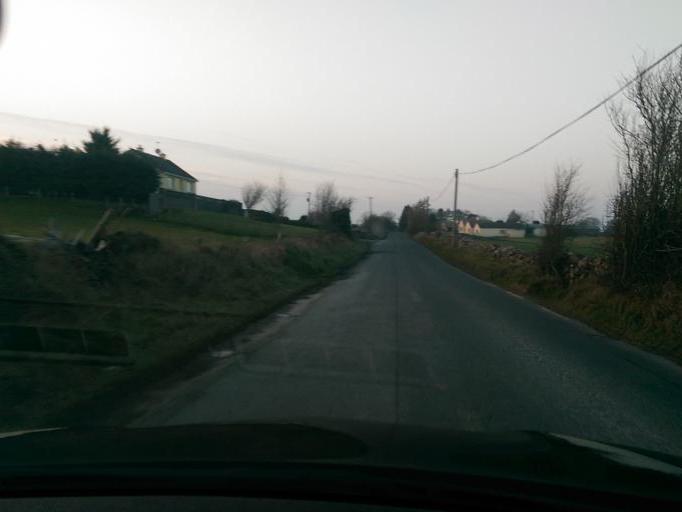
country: IE
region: Connaught
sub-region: County Galway
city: Athenry
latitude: 53.2691
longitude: -8.6923
